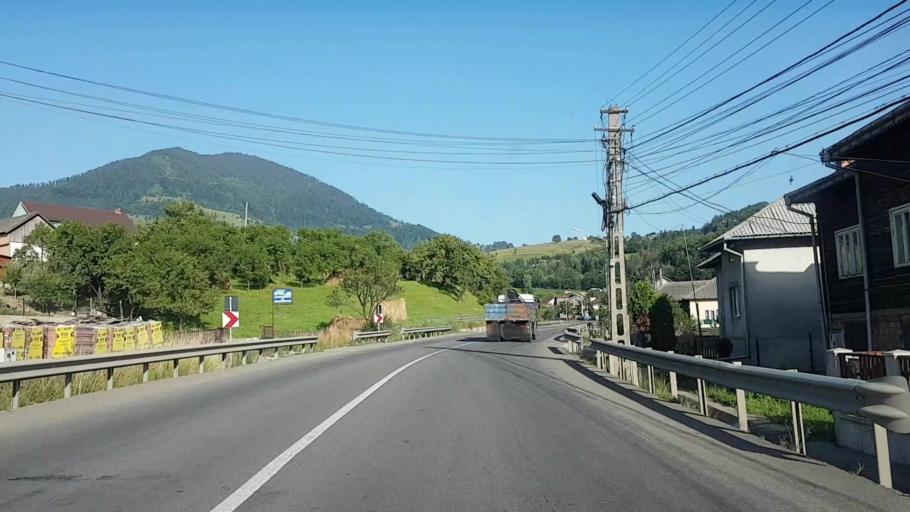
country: RO
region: Bistrita-Nasaud
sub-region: Comuna Tiha Bargaului
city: Tureac
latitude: 47.2122
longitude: 24.8533
